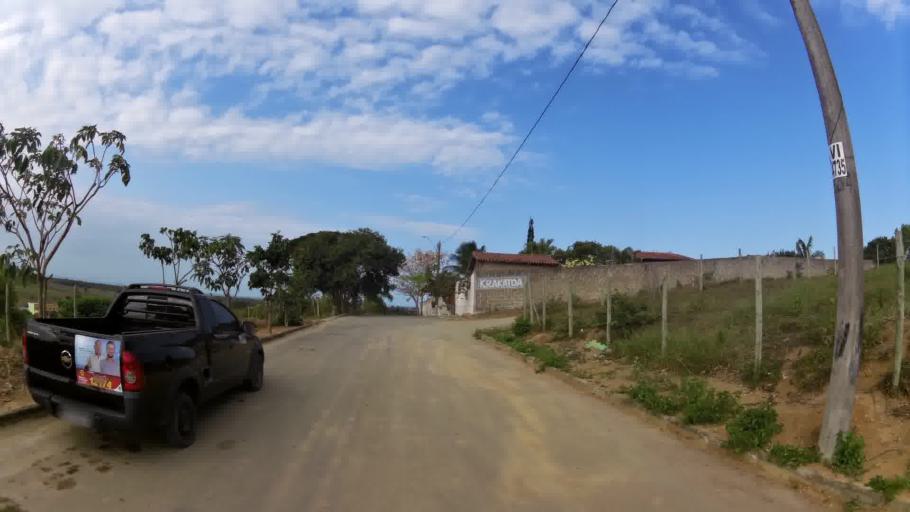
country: BR
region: Espirito Santo
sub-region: Itapemirim
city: Itapemirim
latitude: -21.0119
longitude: -40.8278
